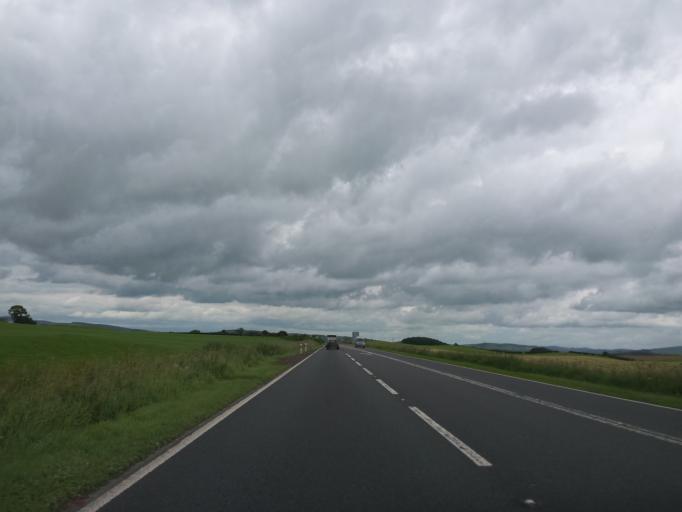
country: GB
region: Scotland
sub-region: Dumfries and Galloway
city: Castle Douglas
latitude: 54.9608
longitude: -3.9132
